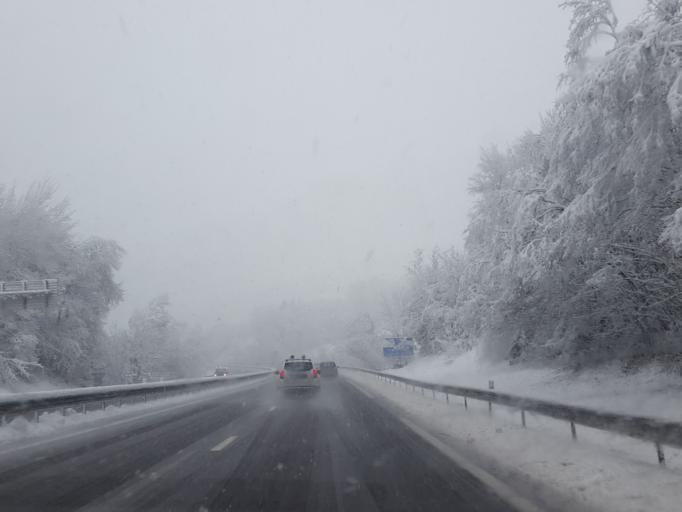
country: FR
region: Rhone-Alpes
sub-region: Departement de la Haute-Savoie
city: Etaux
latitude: 46.0470
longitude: 6.2686
